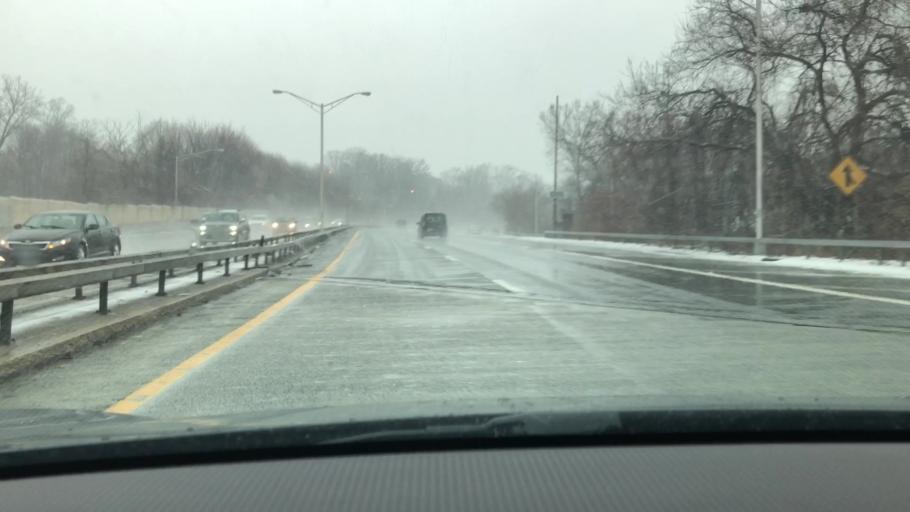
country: US
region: New York
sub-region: Westchester County
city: Pelham
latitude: 40.9344
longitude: -73.8074
